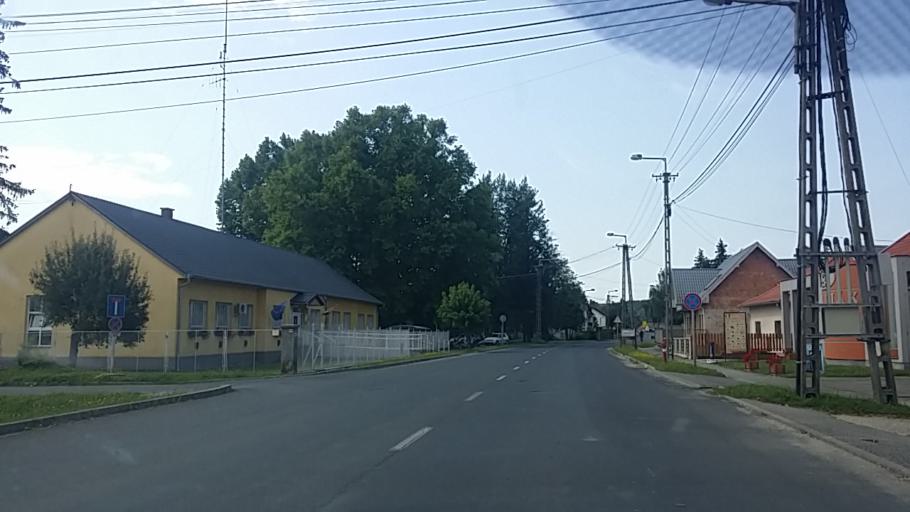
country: HU
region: Zala
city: Lenti
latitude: 46.6224
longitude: 16.5463
